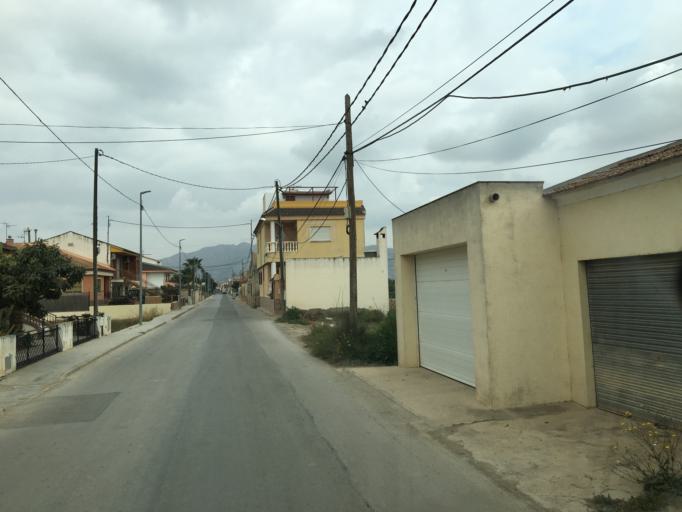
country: ES
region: Murcia
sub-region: Murcia
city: Beniel
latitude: 38.0415
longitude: -0.9905
